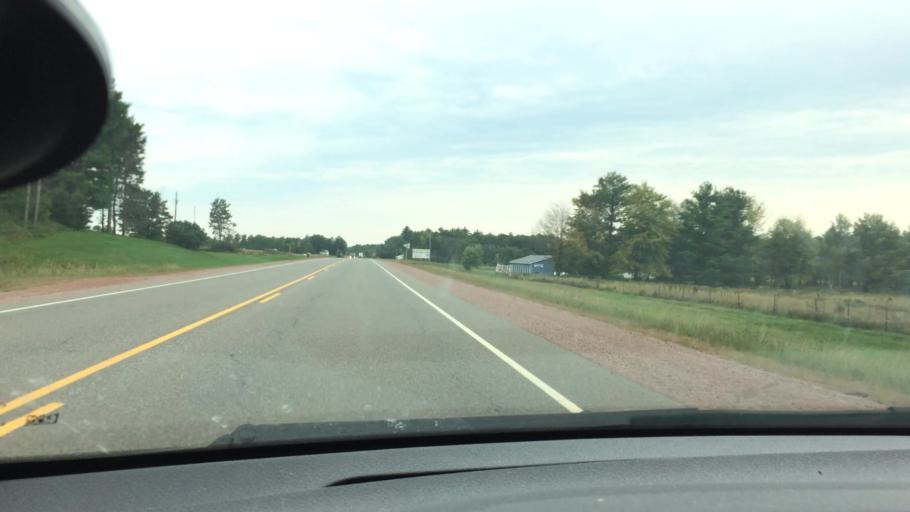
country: US
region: Wisconsin
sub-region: Clark County
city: Neillsville
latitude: 44.5627
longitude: -90.6878
